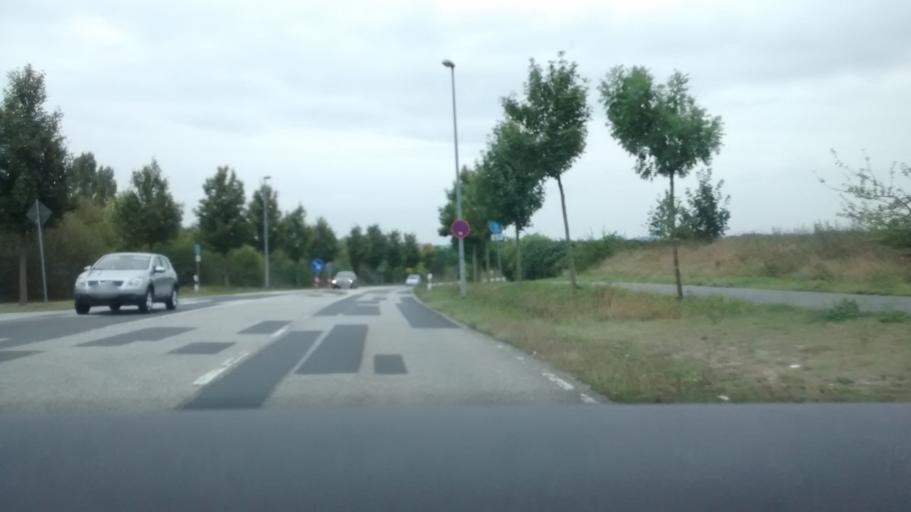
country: DE
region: Mecklenburg-Vorpommern
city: Wismar
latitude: 53.8908
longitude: 11.4252
